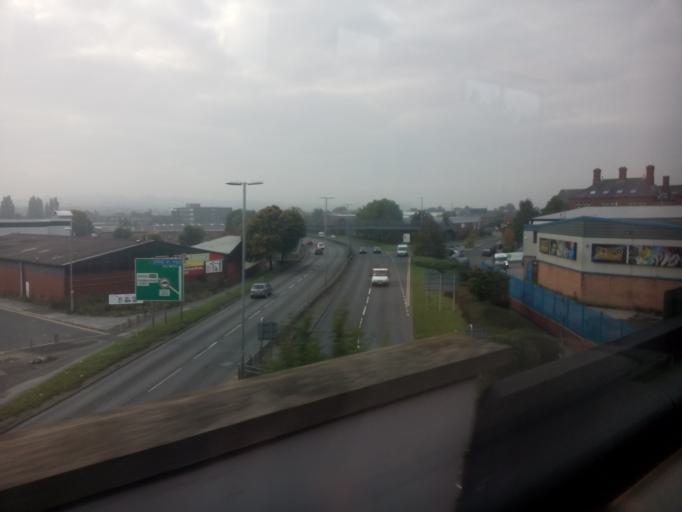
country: GB
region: England
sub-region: City and Borough of Leeds
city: Leeds
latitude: 53.7918
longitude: -1.5669
